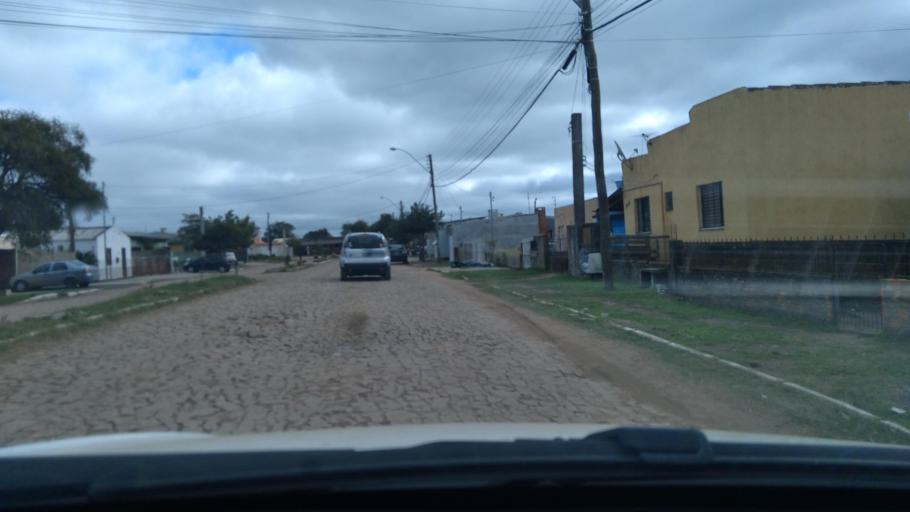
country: BR
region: Rio Grande do Sul
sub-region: Dom Pedrito
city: Dom Pedrito
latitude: -30.9807
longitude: -54.6608
